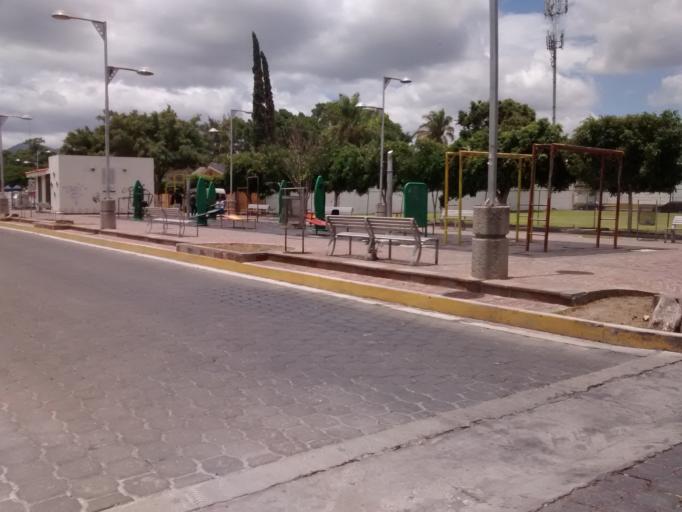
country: MX
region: Puebla
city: Tehuacan
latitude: 18.4516
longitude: -97.3929
